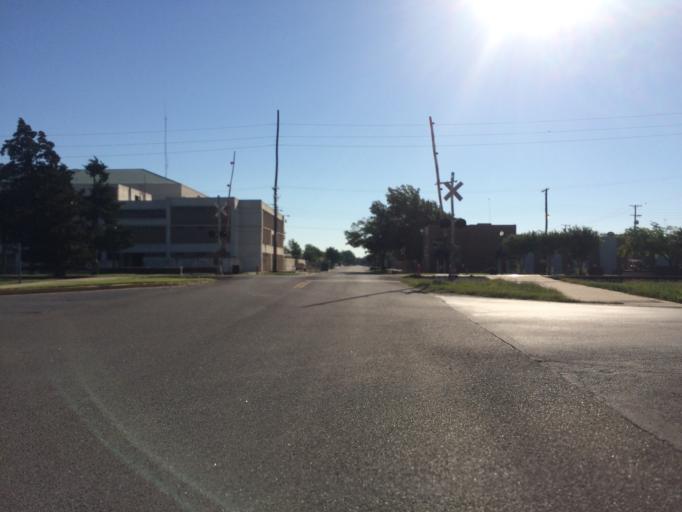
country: US
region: Oklahoma
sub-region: Cleveland County
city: Norman
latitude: 35.2188
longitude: -97.4428
